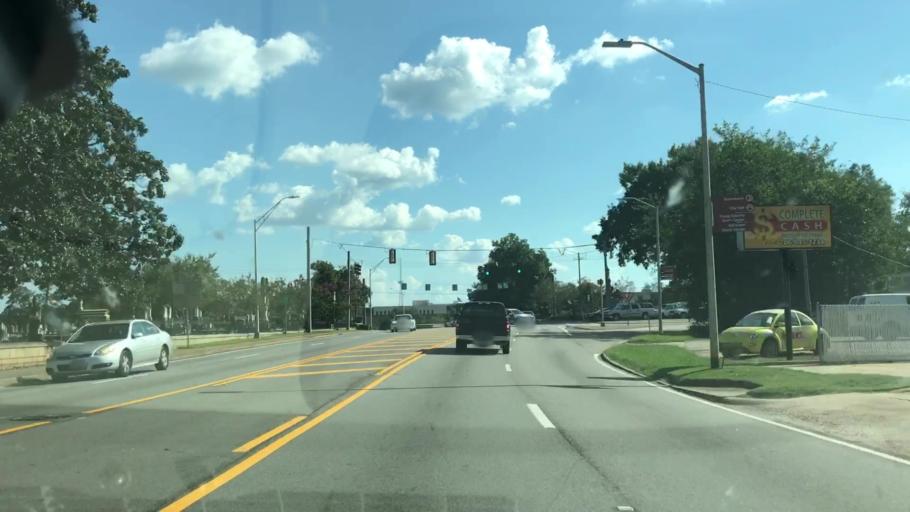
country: US
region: Georgia
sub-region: Troup County
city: La Grange
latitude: 33.0445
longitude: -85.0299
